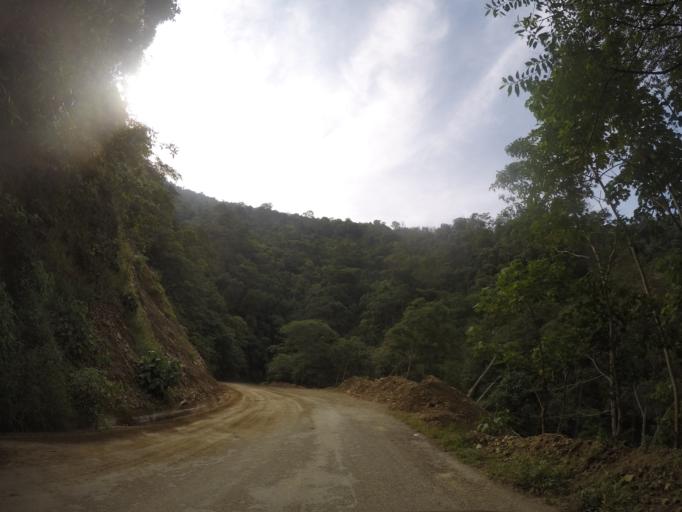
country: MX
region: Oaxaca
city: Pluma Hidalgo
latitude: 15.9474
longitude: -96.4392
